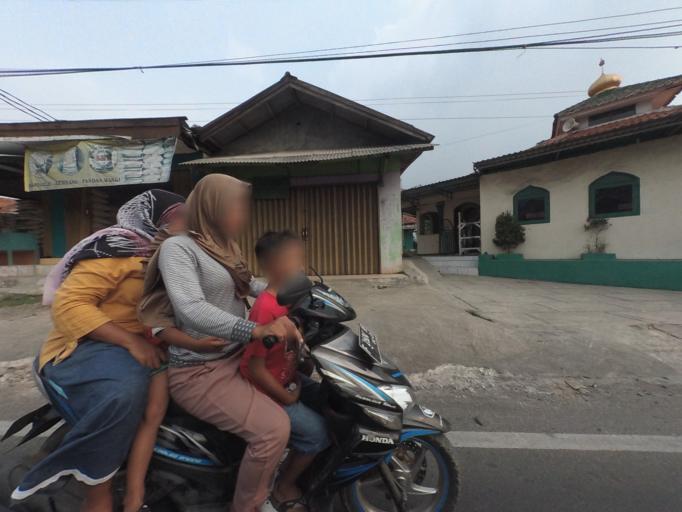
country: ID
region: West Java
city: Ciampea
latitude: -6.5680
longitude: 106.6705
